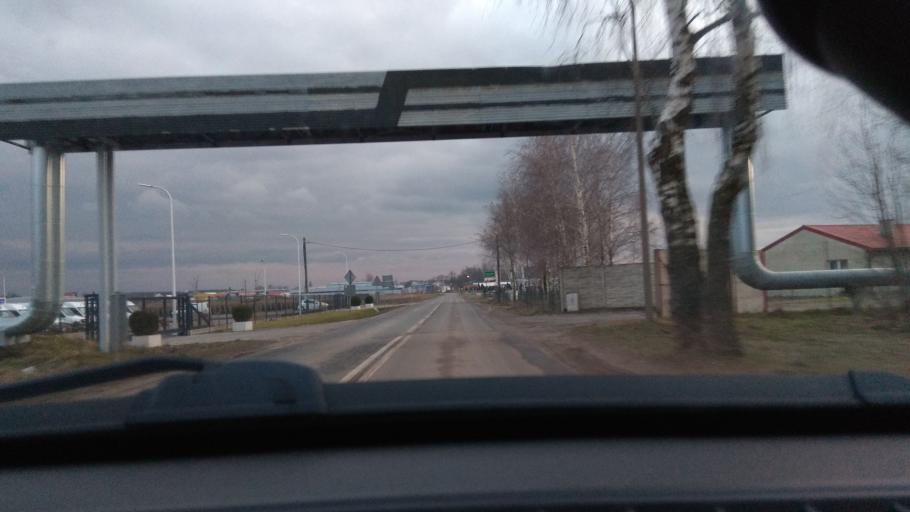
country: PL
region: Greater Poland Voivodeship
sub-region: Powiat kepinski
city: Kepno
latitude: 51.2925
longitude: 18.0061
